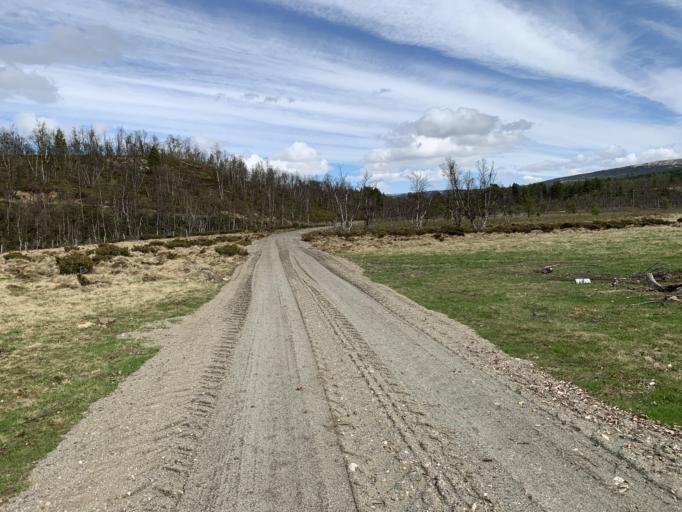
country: NO
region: Hedmark
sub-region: Alvdal
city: Alvdal
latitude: 62.4123
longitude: 10.4022
